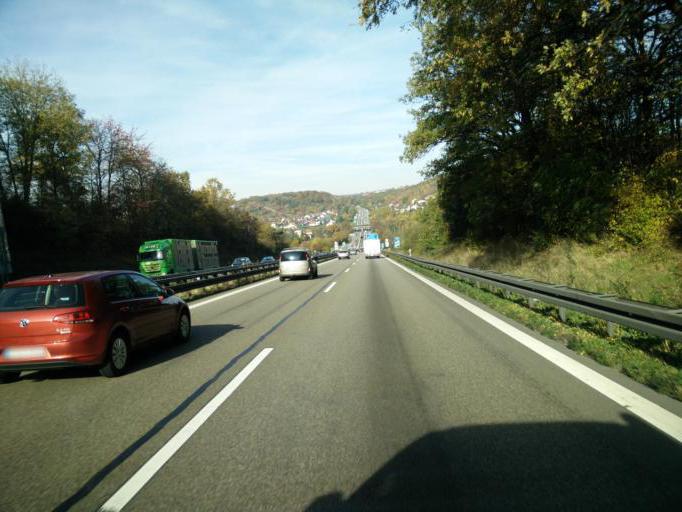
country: DE
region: Baden-Wuerttemberg
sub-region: Karlsruhe Region
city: Niefern-Oschelbronn
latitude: 48.9114
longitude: 8.7684
